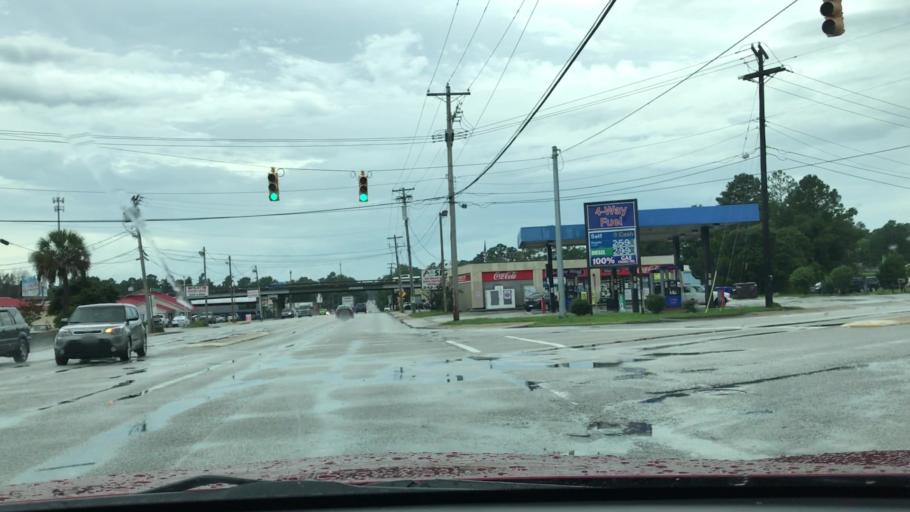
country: US
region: South Carolina
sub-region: Horry County
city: Conway
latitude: 33.8319
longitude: -79.0565
